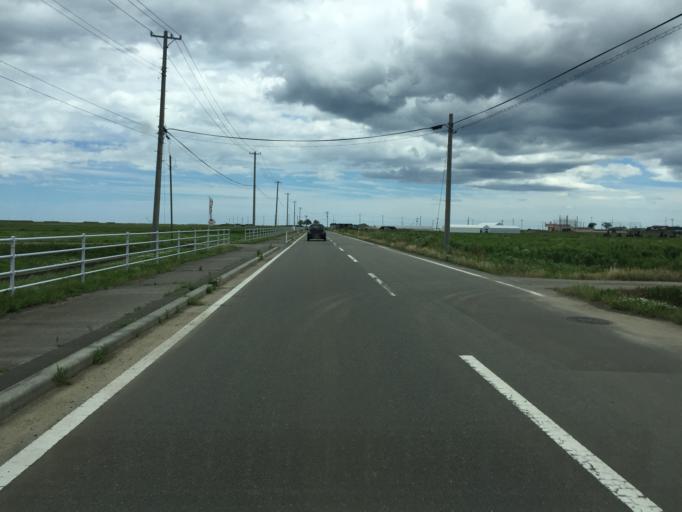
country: JP
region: Fukushima
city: Namie
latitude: 37.6982
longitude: 140.9864
